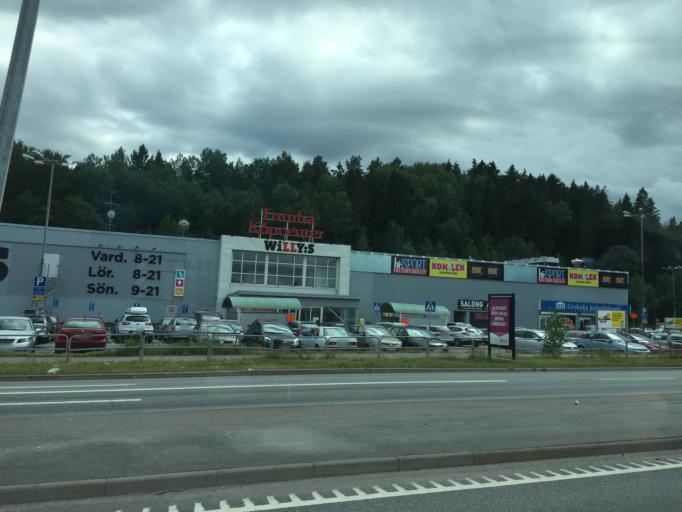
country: SE
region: Stockholm
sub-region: Botkyrka Kommun
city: Tumba
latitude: 59.1992
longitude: 17.8441
